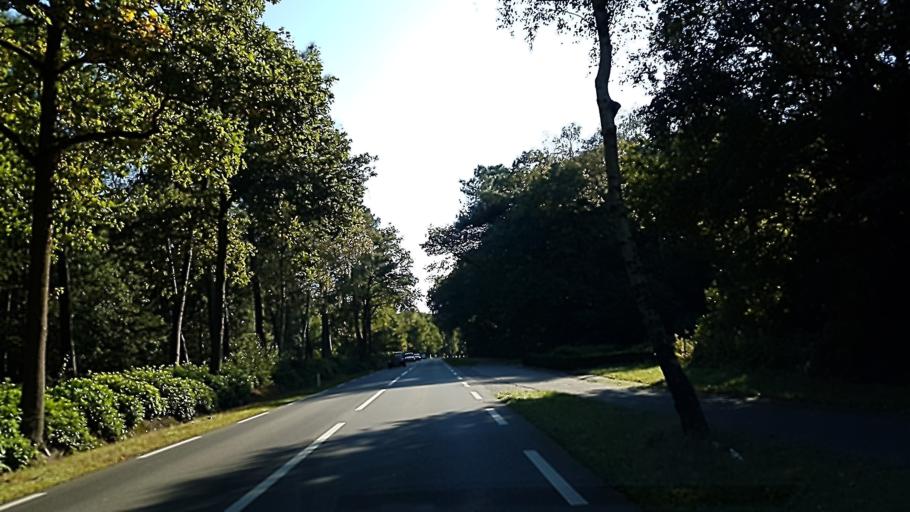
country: NL
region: North Brabant
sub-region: Gemeente Woensdrecht
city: Woensdrecht
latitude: 51.4020
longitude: 4.3551
